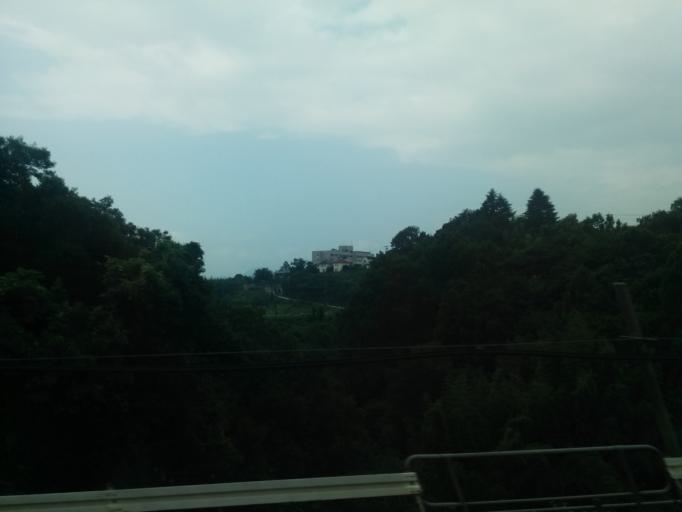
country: JP
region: Shizuoka
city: Mishima
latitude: 35.1217
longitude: 138.9416
